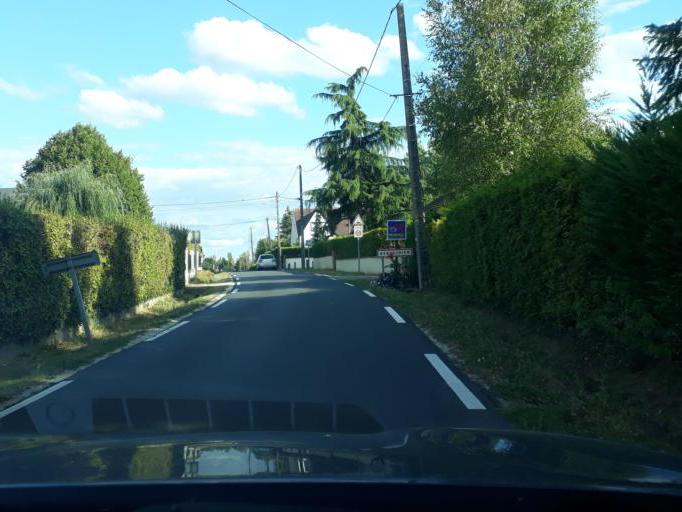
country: FR
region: Centre
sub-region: Departement du Loiret
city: Rebrechien
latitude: 47.9875
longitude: 2.0299
